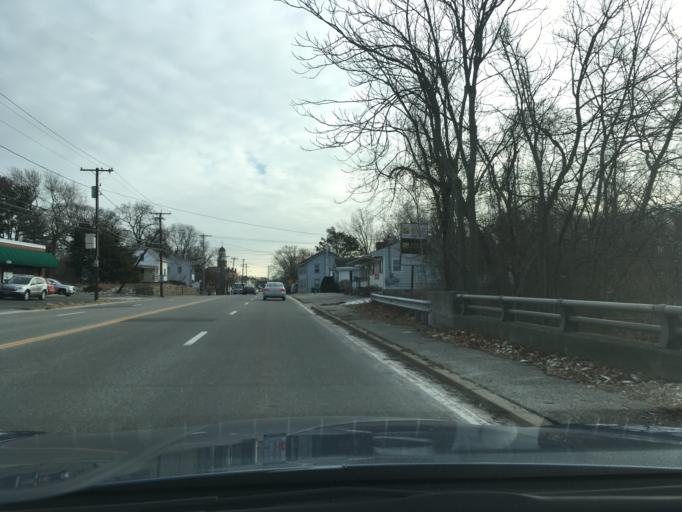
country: US
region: Rhode Island
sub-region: Kent County
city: East Greenwich
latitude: 41.7035
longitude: -71.4615
